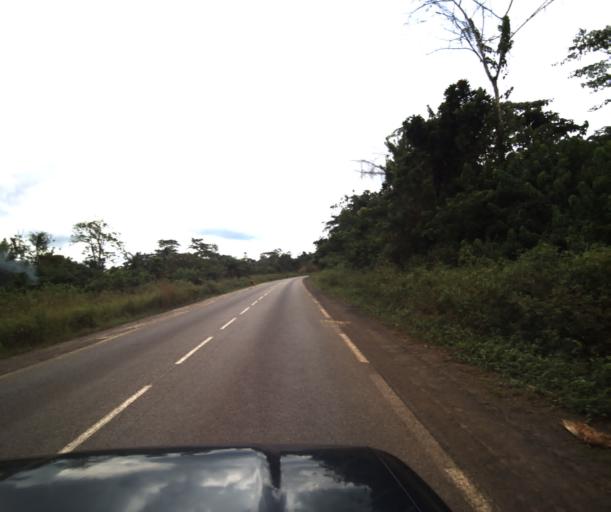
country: CM
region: Littoral
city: Edea
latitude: 3.8253
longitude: 10.3868
